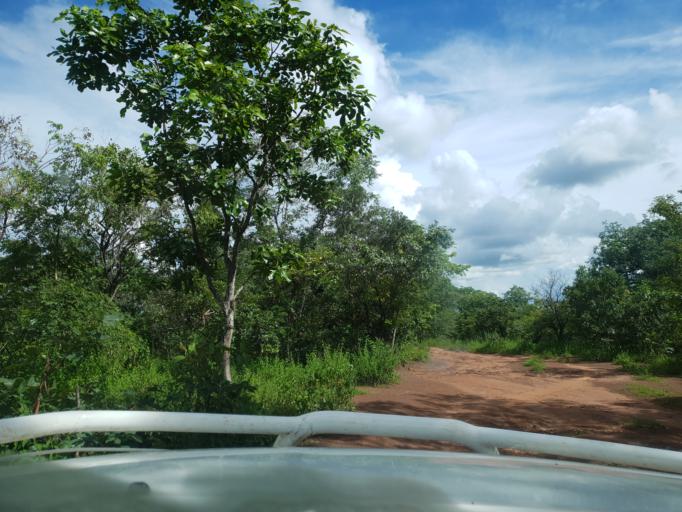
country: CI
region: Savanes
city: Tengrela
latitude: 10.4605
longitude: -6.7962
